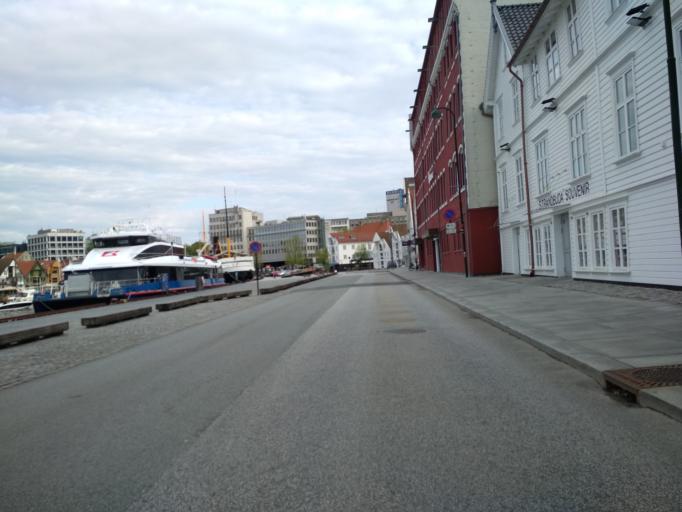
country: NO
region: Rogaland
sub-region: Stavanger
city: Stavanger
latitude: 58.9718
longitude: 5.7277
